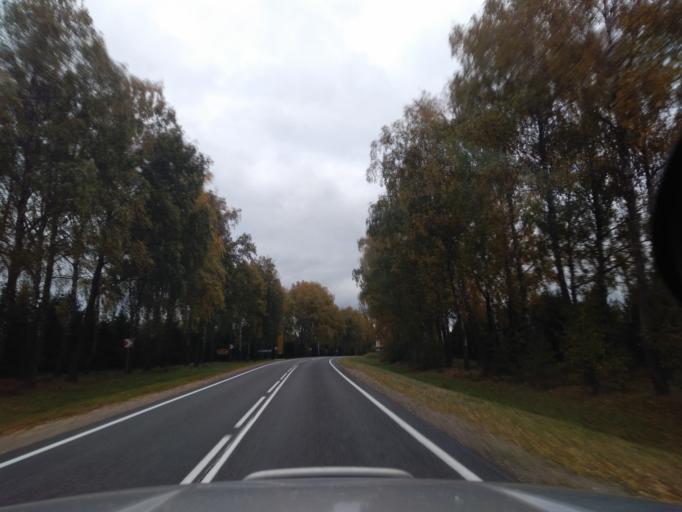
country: BY
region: Minsk
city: Slutsk
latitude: 53.2218
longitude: 27.4946
